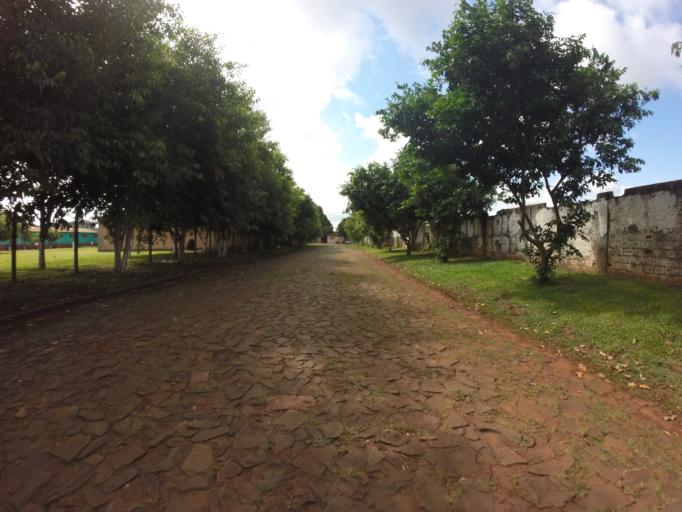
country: PY
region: Alto Parana
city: Ciudad del Este
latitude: -25.4019
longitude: -54.6454
